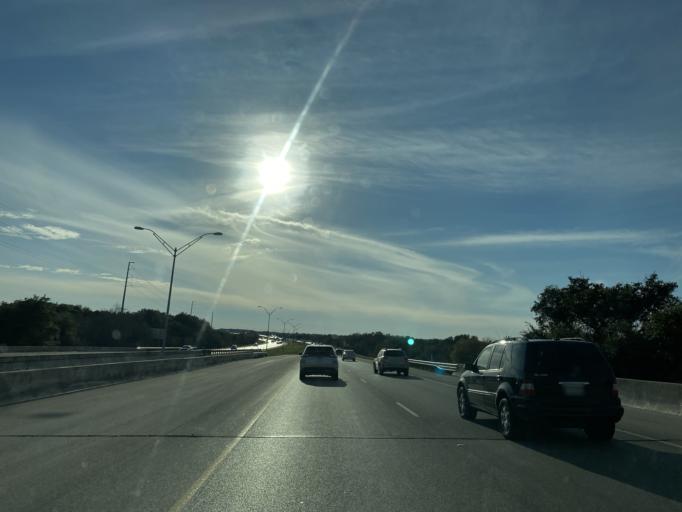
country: US
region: Texas
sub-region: Travis County
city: Shady Hollow
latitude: 30.2159
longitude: -97.8525
